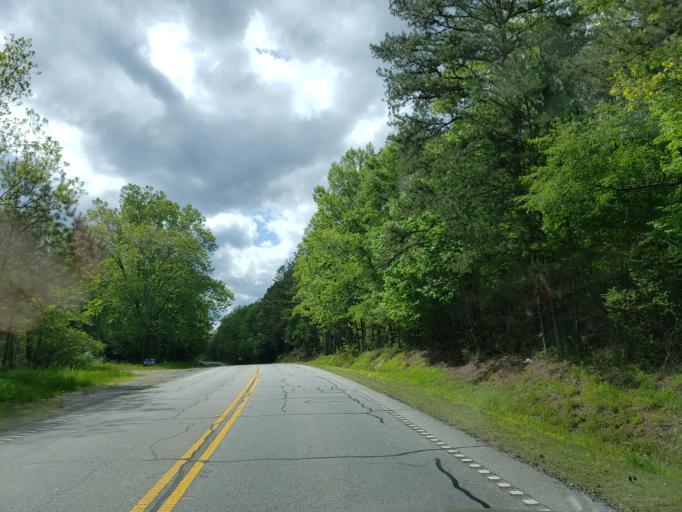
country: US
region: Georgia
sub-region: Haralson County
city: Tallapoosa
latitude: 33.7444
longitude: -85.3421
